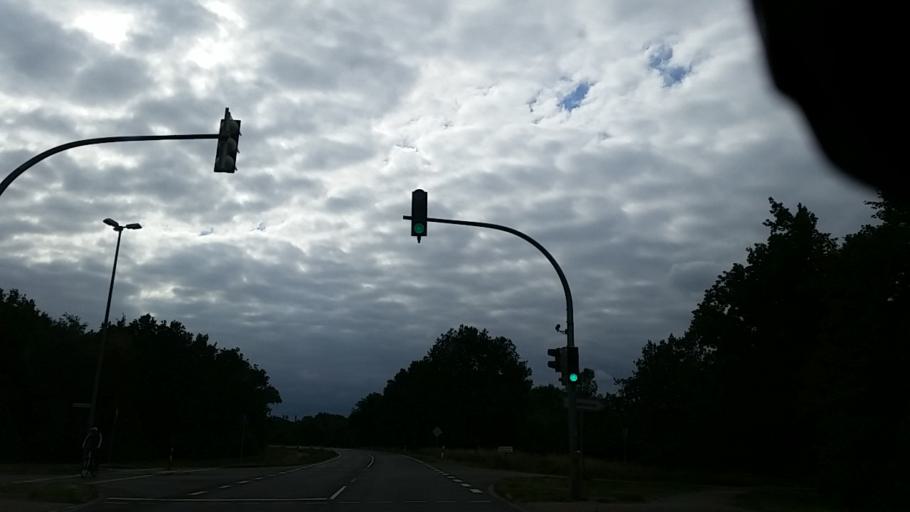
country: DE
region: Lower Saxony
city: Wolfsburg
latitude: 52.4266
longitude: 10.8422
